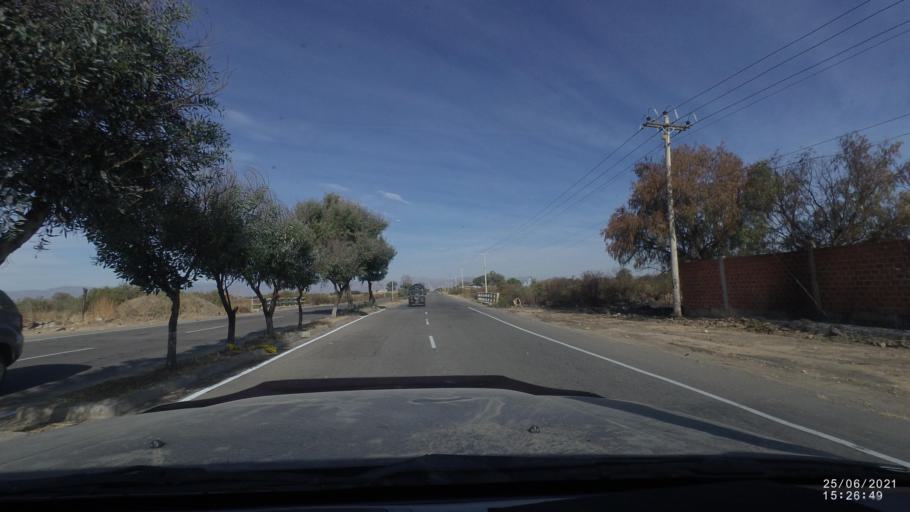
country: BO
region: Cochabamba
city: Cliza
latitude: -17.5426
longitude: -65.9554
